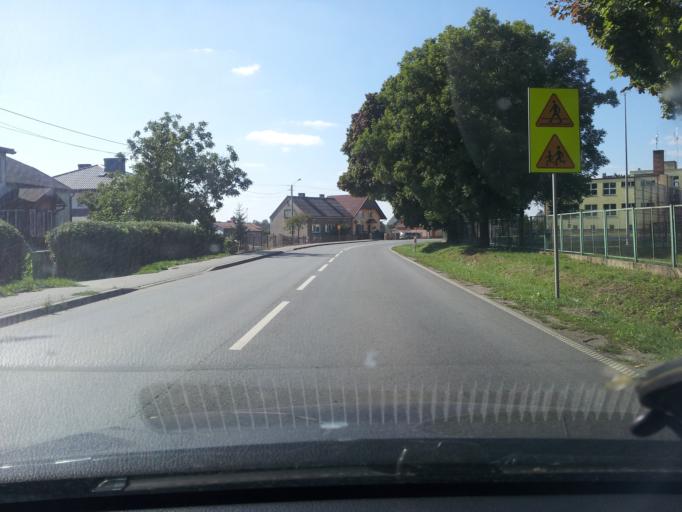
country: PL
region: Kujawsko-Pomorskie
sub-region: Powiat rypinski
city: Ostrowite
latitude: 53.0691
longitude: 19.2974
